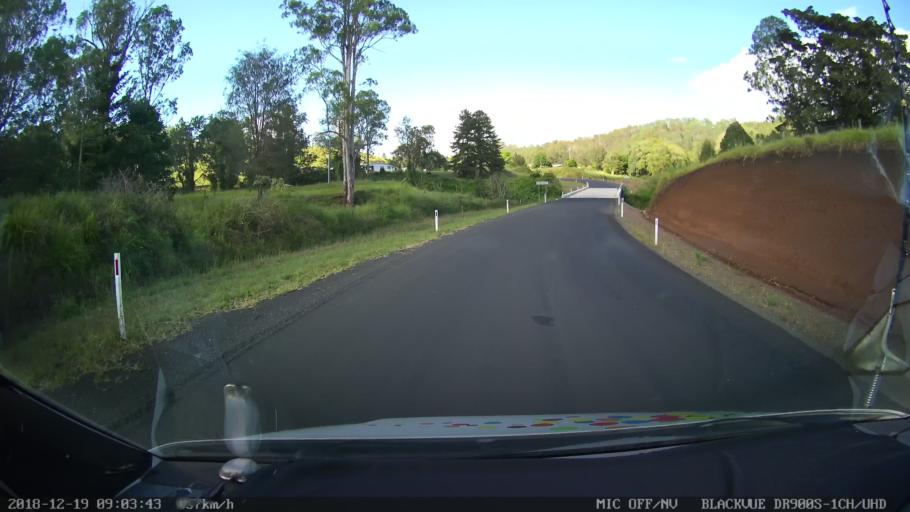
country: AU
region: New South Wales
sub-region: Kyogle
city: Kyogle
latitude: -28.4500
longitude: 152.9498
